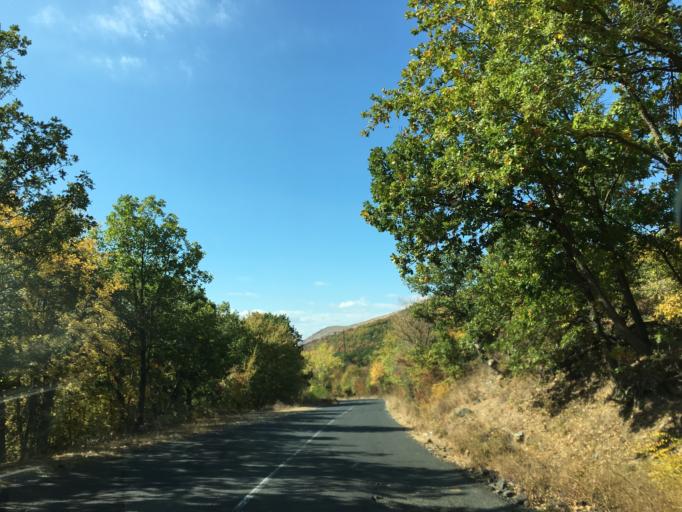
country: BG
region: Kurdzhali
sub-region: Obshtina Kurdzhali
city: Kurdzhali
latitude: 41.5282
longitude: 25.4596
